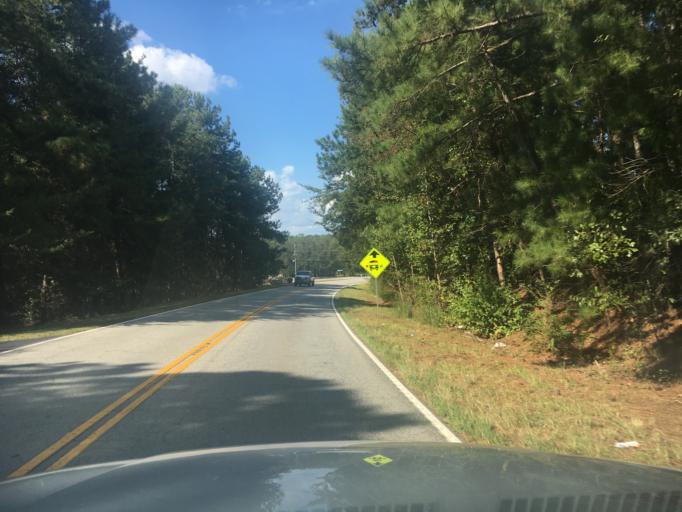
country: US
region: South Carolina
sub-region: Anderson County
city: Pendleton
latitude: 34.5533
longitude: -82.8098
